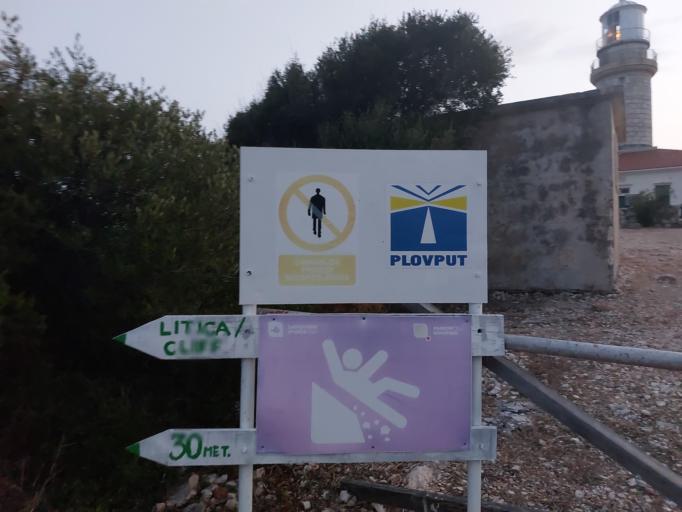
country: HR
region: Dubrovacko-Neretvanska
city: Smokvica
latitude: 42.7245
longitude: 16.8852
